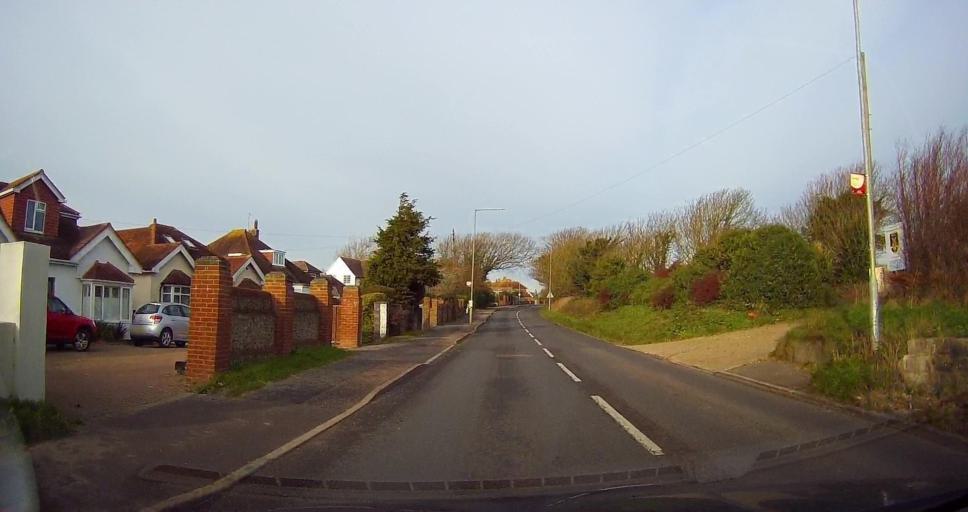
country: GB
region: England
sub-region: Brighton and Hove
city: Rottingdean
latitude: 50.8108
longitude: -0.0606
